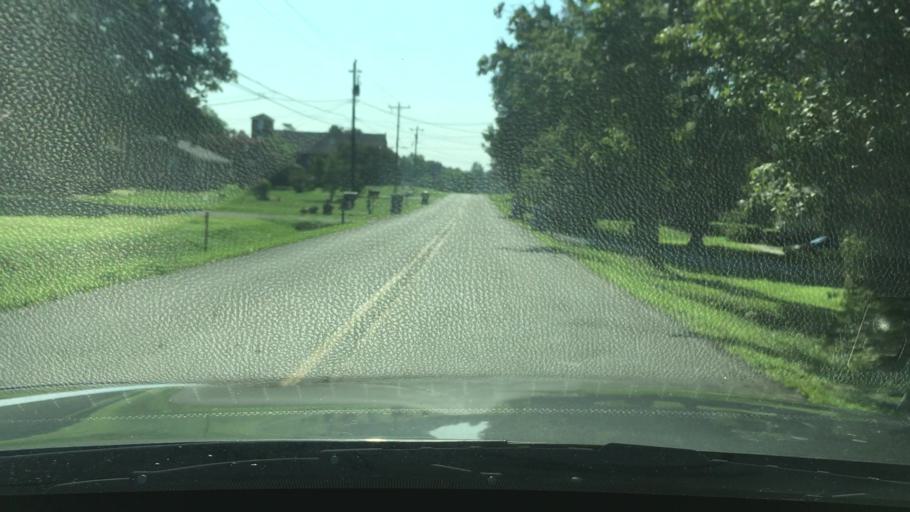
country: US
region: North Carolina
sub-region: Alamance County
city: Green Level
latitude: 36.1168
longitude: -79.3491
